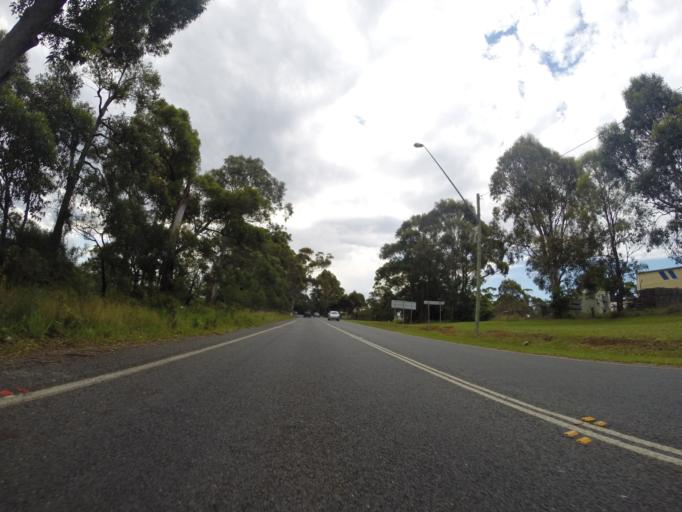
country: AU
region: New South Wales
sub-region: Shoalhaven Shire
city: Ulladulla
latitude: -35.3417
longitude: 150.4640
